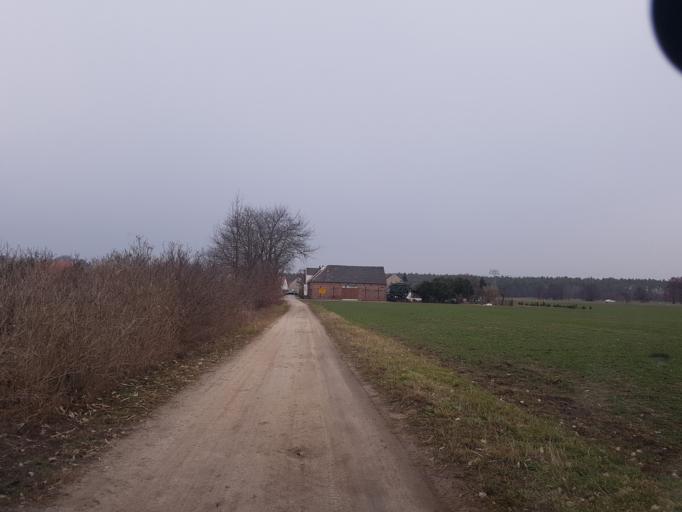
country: DE
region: Brandenburg
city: Finsterwalde
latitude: 51.6616
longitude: 13.6866
